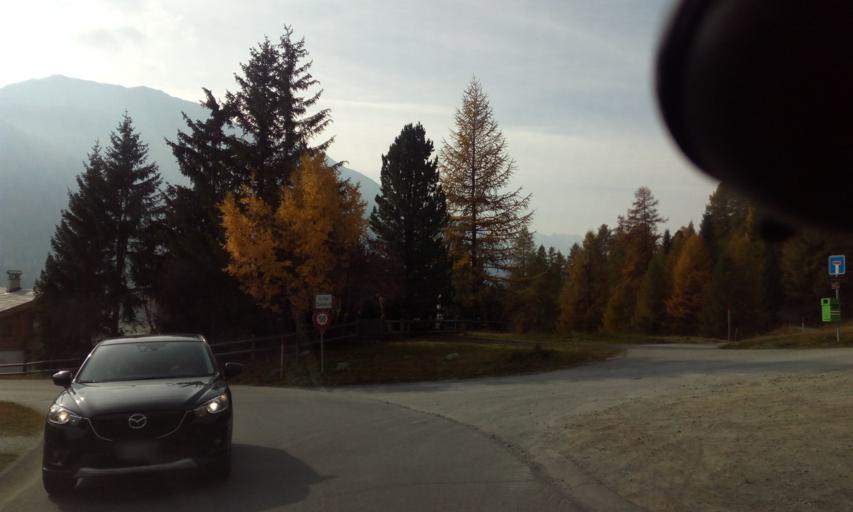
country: CH
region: Grisons
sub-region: Maloja District
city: Ponte
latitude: 46.5800
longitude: 9.9194
